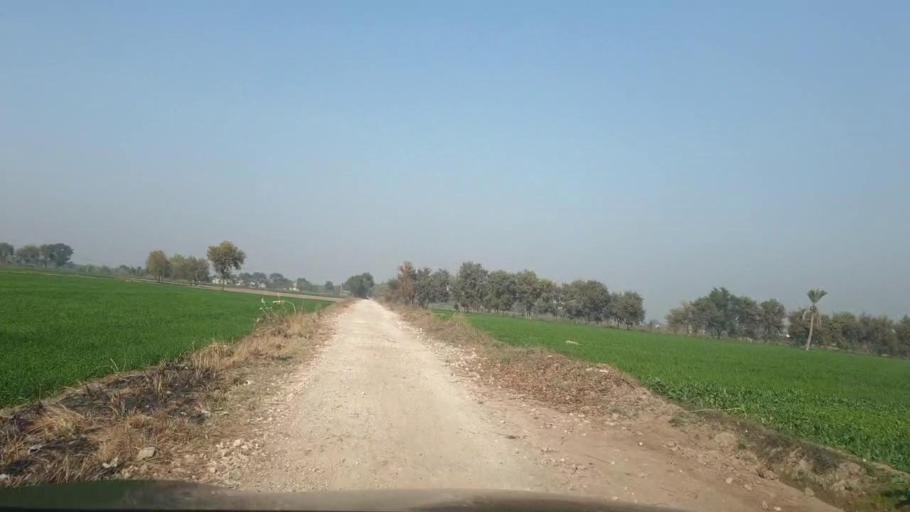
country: PK
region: Sindh
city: Ubauro
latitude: 28.0897
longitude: 69.8412
